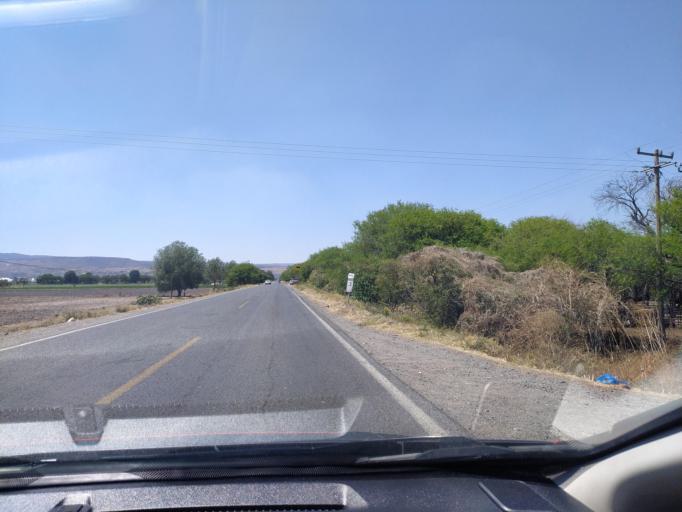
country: MX
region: Guanajuato
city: Ciudad Manuel Doblado
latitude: 20.7408
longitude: -101.9200
